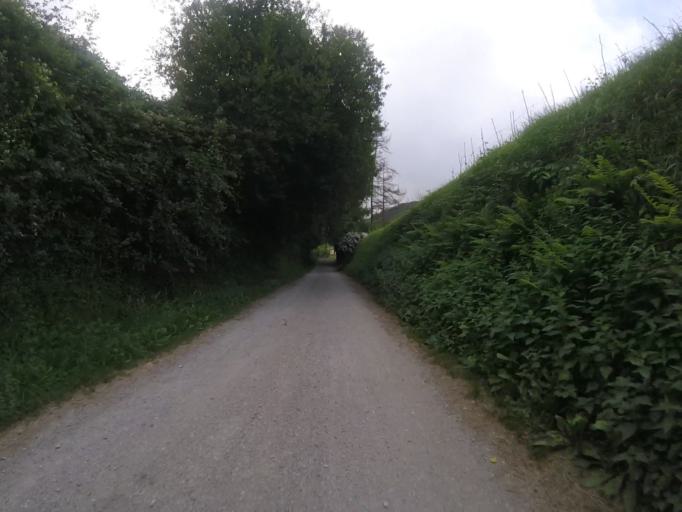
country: ES
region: Navarre
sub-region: Provincia de Navarra
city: Leitza
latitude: 43.0857
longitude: -1.9141
